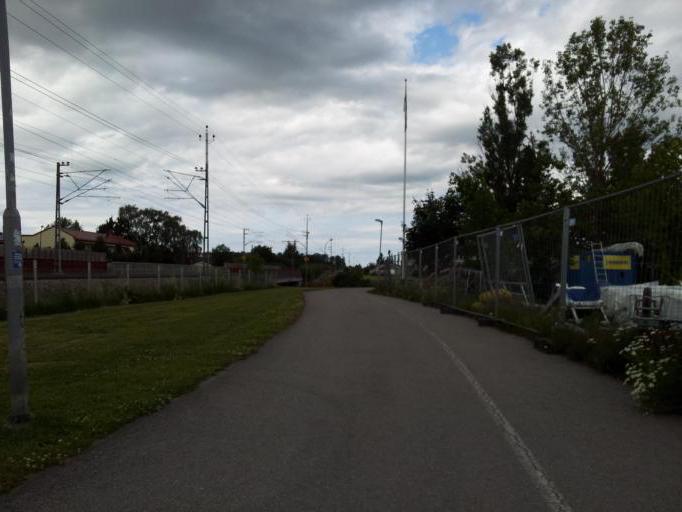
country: SE
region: Uppsala
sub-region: Uppsala Kommun
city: Uppsala
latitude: 59.8719
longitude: 17.6360
